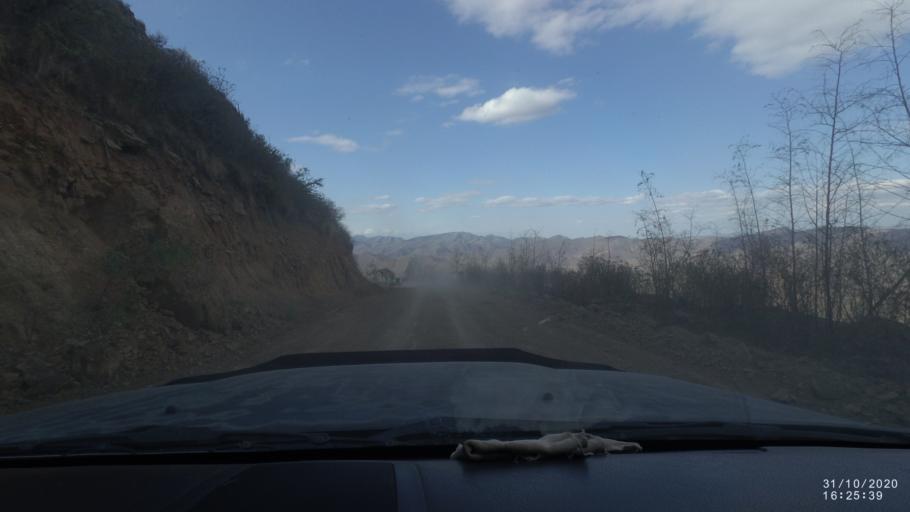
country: BO
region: Chuquisaca
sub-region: Provincia Zudanez
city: Mojocoya
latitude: -18.3995
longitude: -64.5872
